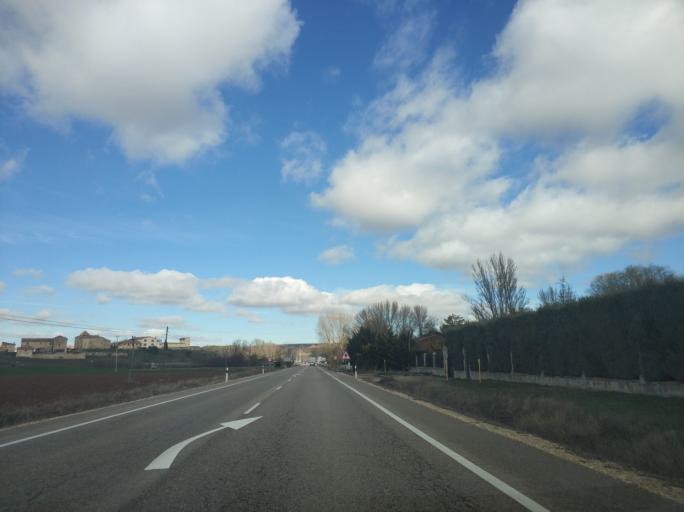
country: ES
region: Castille and Leon
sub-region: Provincia de Burgos
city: Saldana de Burgos
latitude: 42.2571
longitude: -3.6926
